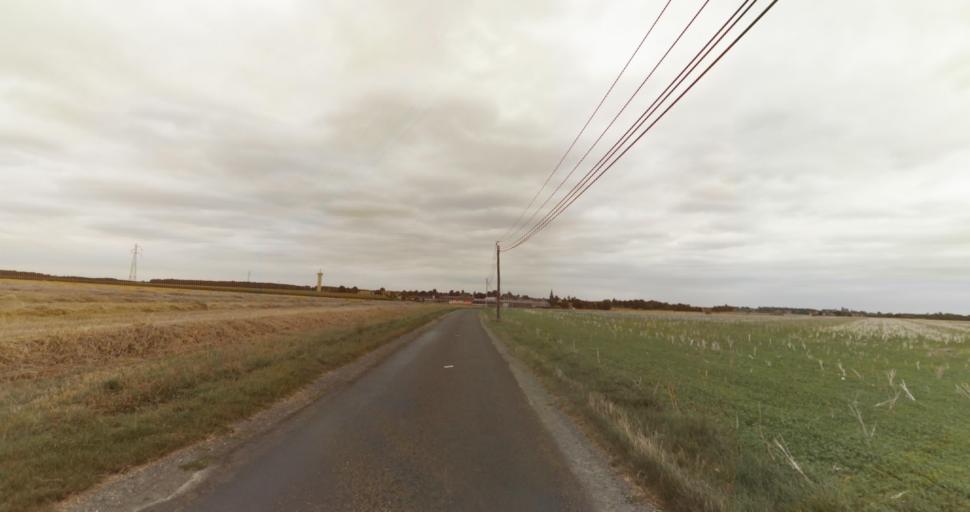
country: FR
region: Haute-Normandie
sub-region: Departement de l'Eure
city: Menilles
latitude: 48.9589
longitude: 1.2802
